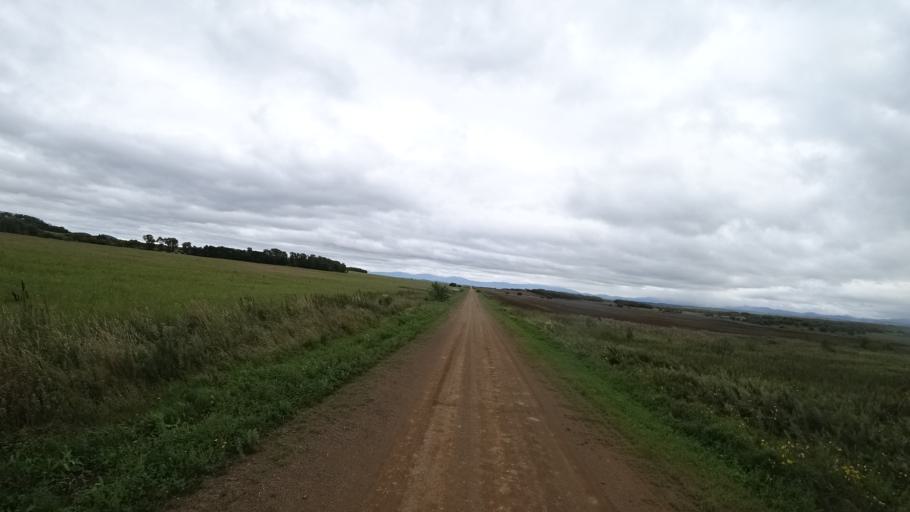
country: RU
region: Primorskiy
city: Chernigovka
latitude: 44.4378
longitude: 132.5777
